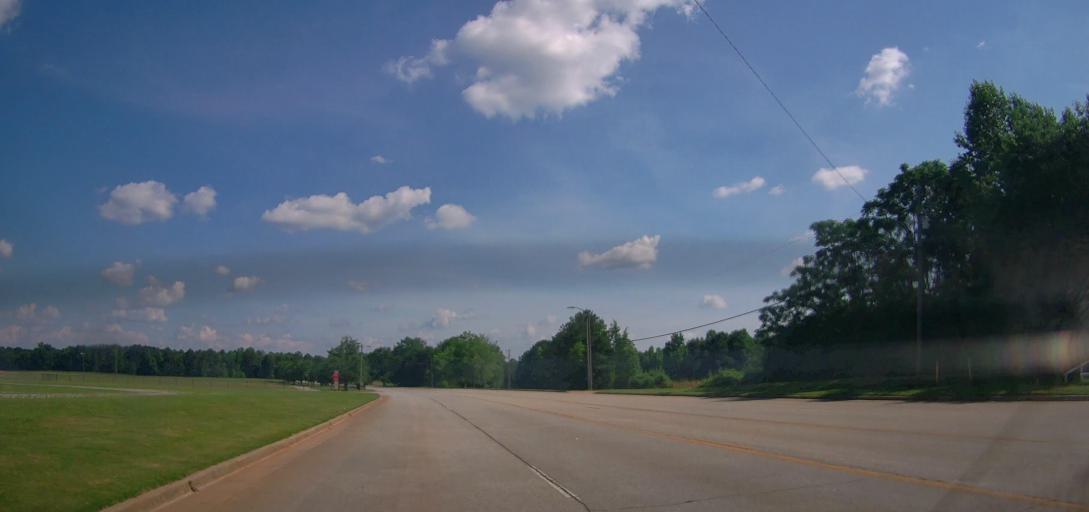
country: US
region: Georgia
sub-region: Henry County
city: Hampton
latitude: 33.3828
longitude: -84.3247
